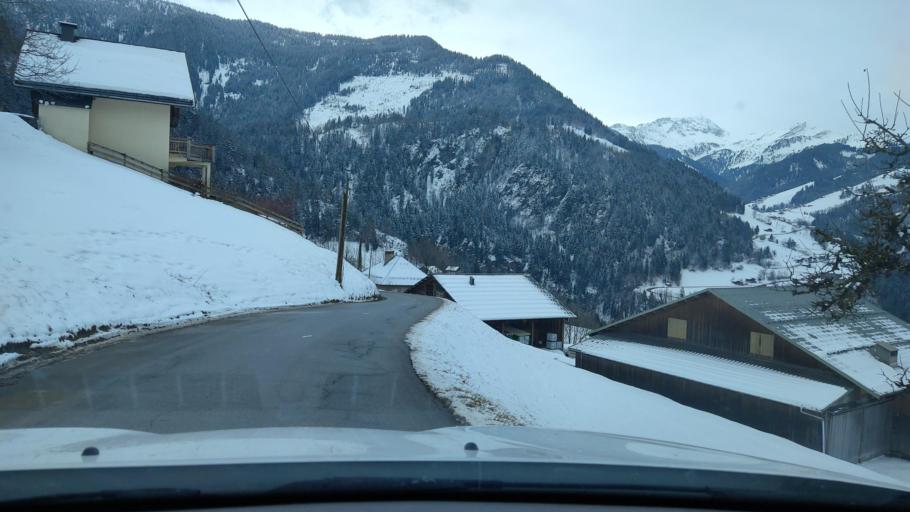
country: FR
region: Rhone-Alpes
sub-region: Departement de la Savoie
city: Beaufort
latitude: 45.7229
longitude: 6.5790
